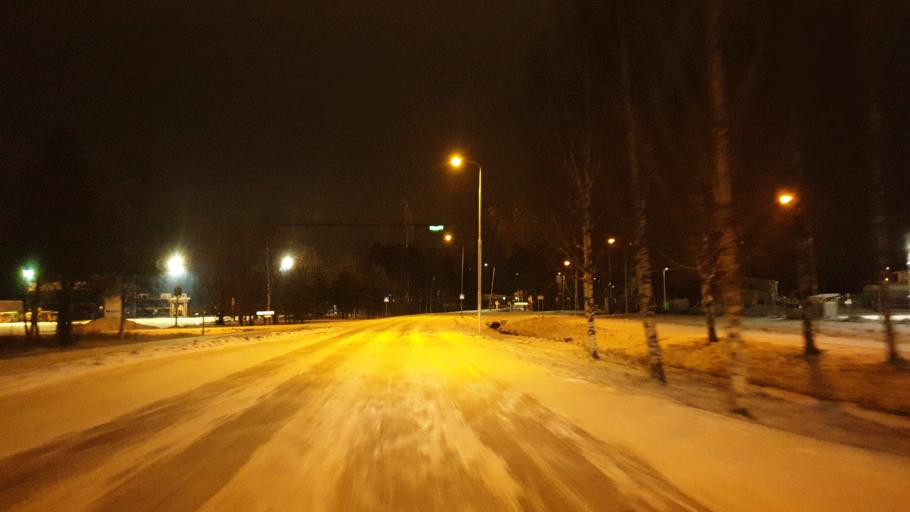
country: FI
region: Northern Ostrobothnia
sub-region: Oulu
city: Oulu
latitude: 64.9944
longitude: 25.4504
